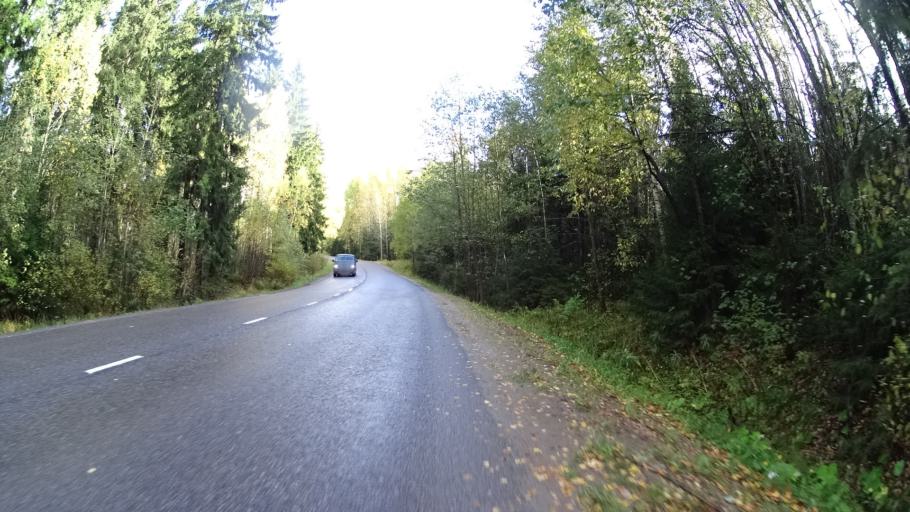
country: FI
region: Uusimaa
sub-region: Helsinki
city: Kilo
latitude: 60.2879
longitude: 24.8085
